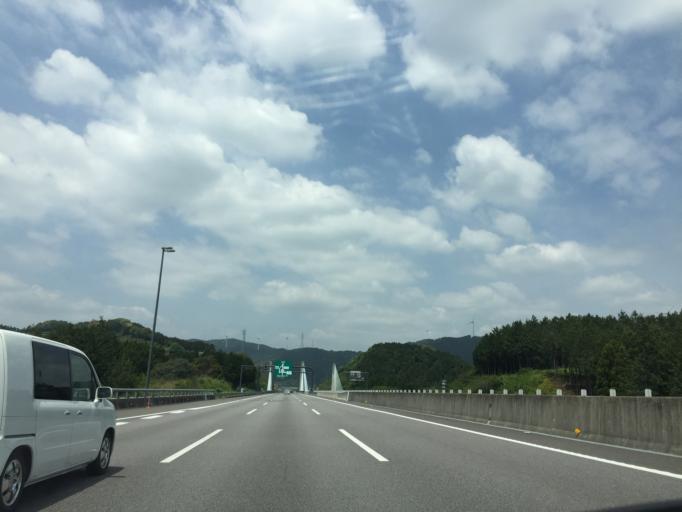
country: JP
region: Shizuoka
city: Hamakita
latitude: 34.8460
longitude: 137.7350
